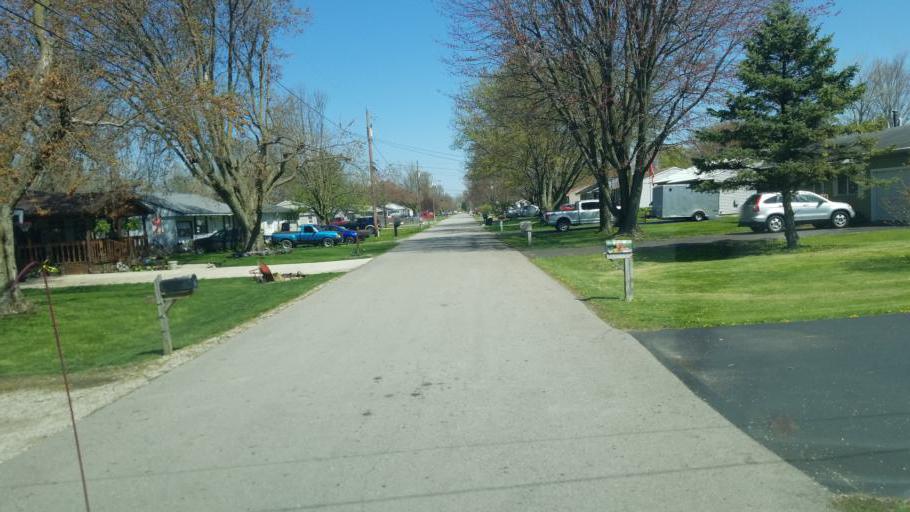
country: US
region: Ohio
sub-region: Marion County
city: Marion
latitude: 40.6365
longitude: -83.0803
